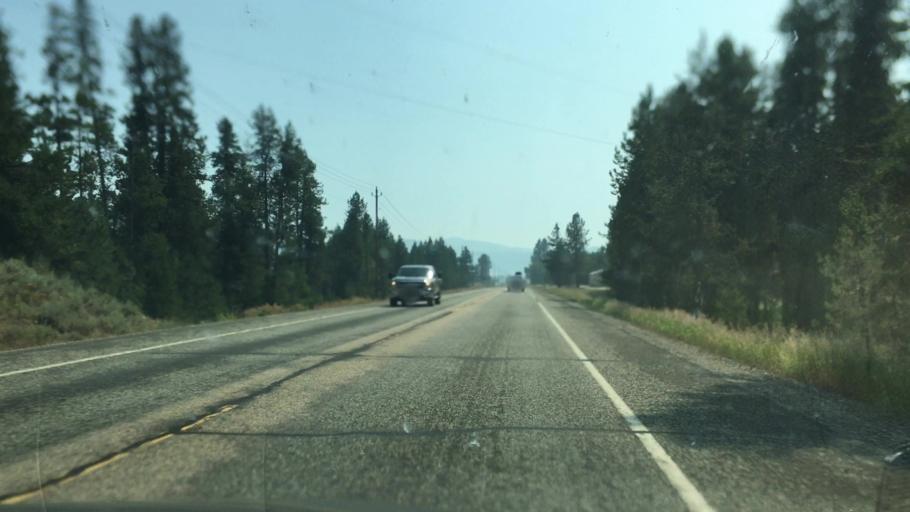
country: US
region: Idaho
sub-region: Valley County
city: Cascade
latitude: 44.3671
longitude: -116.0182
